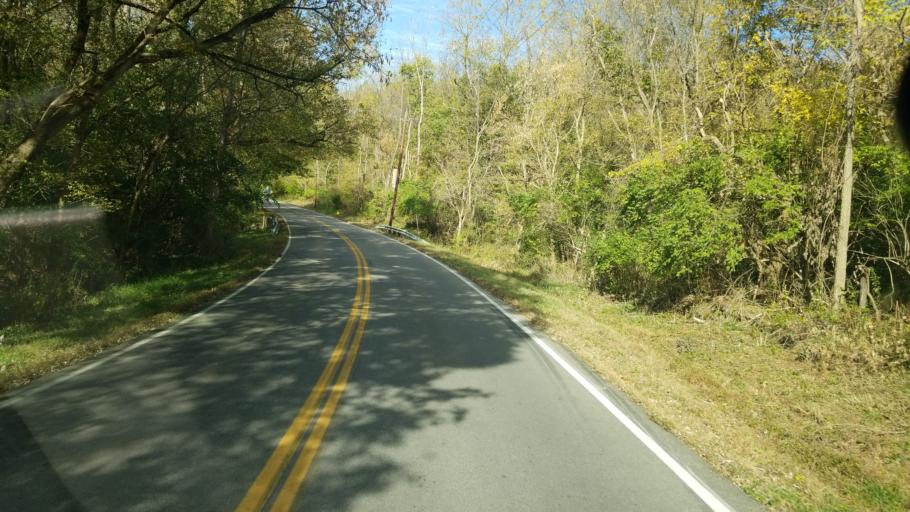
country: US
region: Ohio
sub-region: Warren County
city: Morrow
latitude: 39.3647
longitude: -84.1471
